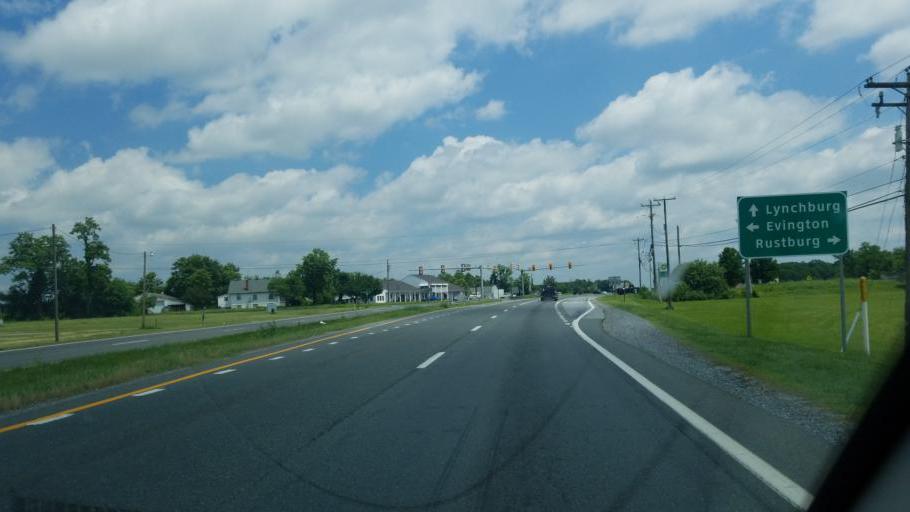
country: US
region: Virginia
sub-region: Campbell County
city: Rustburg
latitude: 37.2522
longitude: -79.1869
